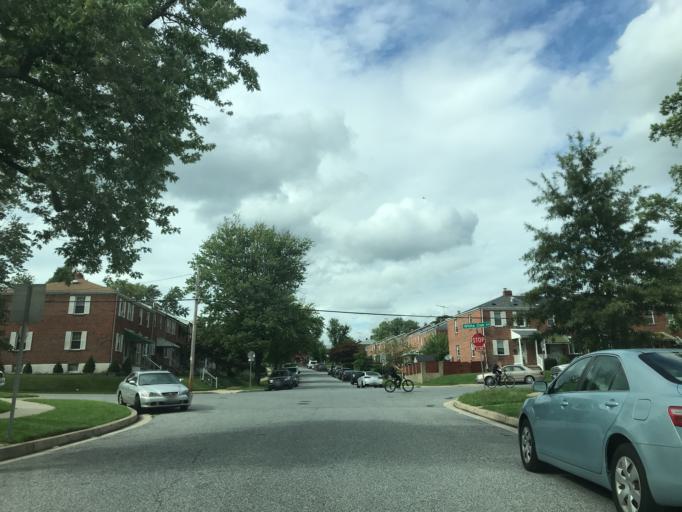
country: US
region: Maryland
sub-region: Baltimore County
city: Parkville
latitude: 39.3947
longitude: -76.5610
